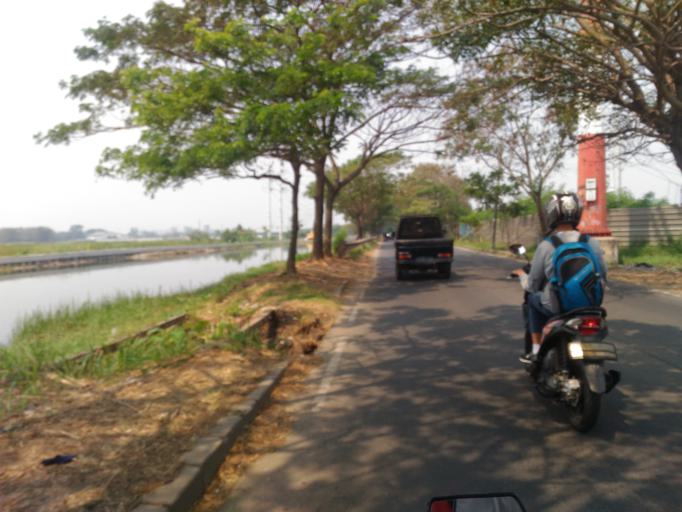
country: ID
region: Banten
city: Tangerang
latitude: -6.1545
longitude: 106.6062
